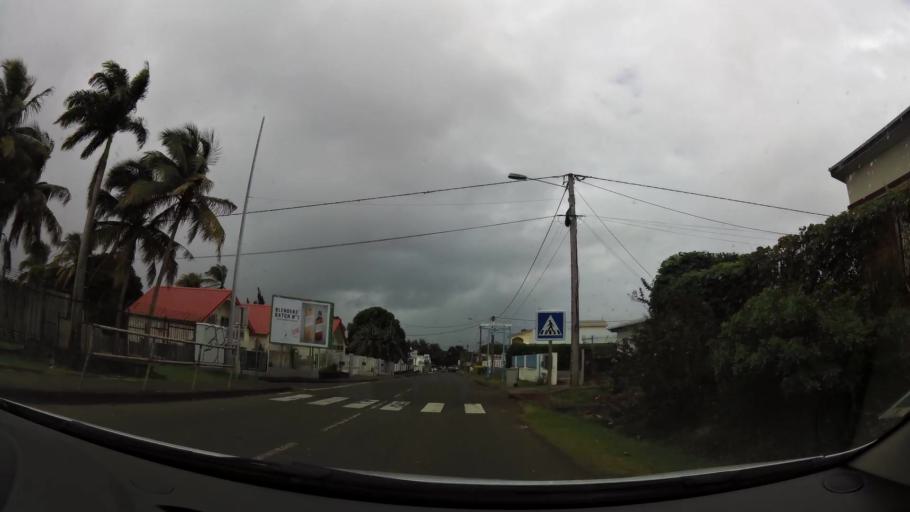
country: RE
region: Reunion
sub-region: Reunion
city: Sainte-Suzanne
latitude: -20.9029
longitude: 55.5989
